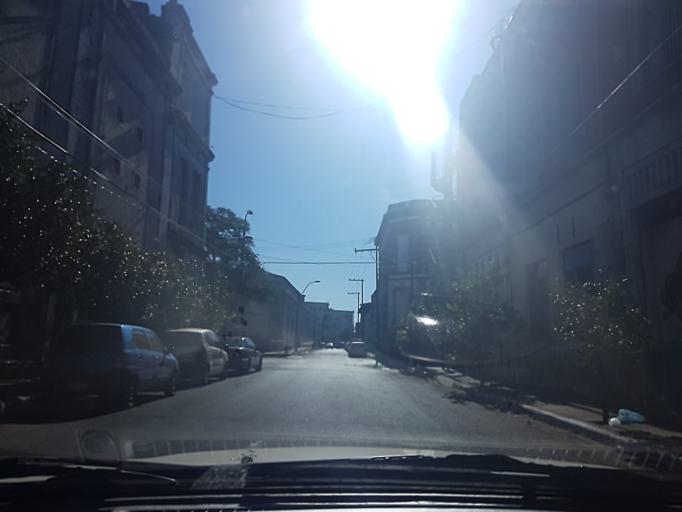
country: PY
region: Asuncion
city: Asuncion
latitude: -25.2779
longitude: -57.6427
